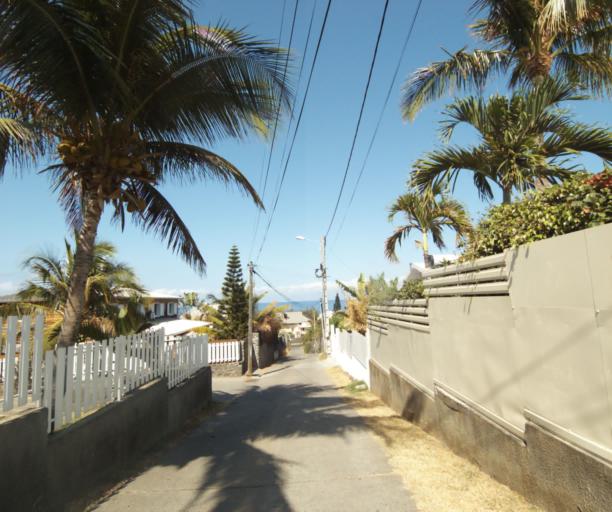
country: RE
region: Reunion
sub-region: Reunion
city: Trois-Bassins
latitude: -21.1047
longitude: 55.2509
